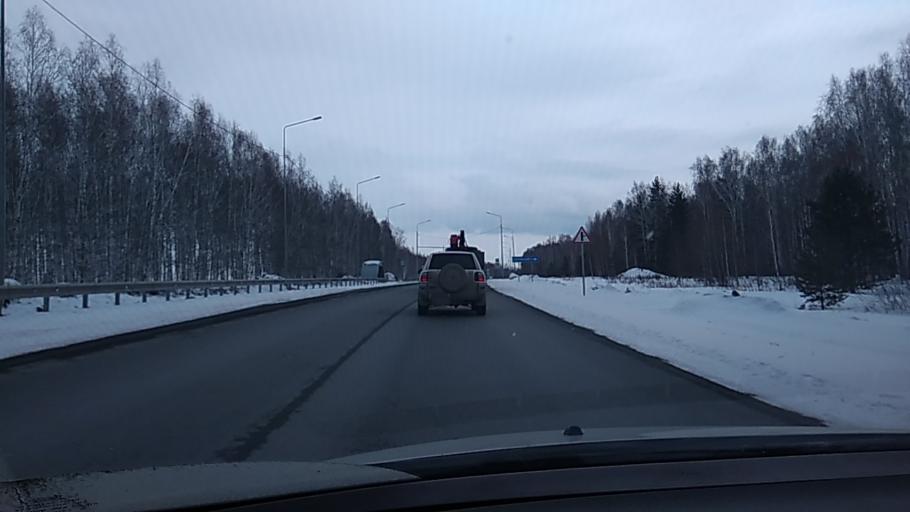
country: RU
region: Sverdlovsk
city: Sovkhoznyy
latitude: 56.5222
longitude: 61.4354
